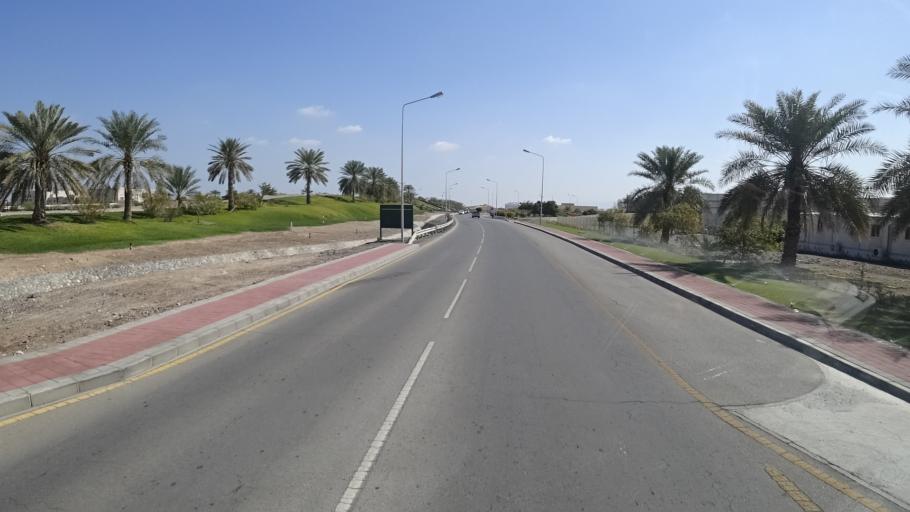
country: OM
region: Muhafazat Masqat
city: As Sib al Jadidah
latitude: 23.5869
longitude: 58.1745
